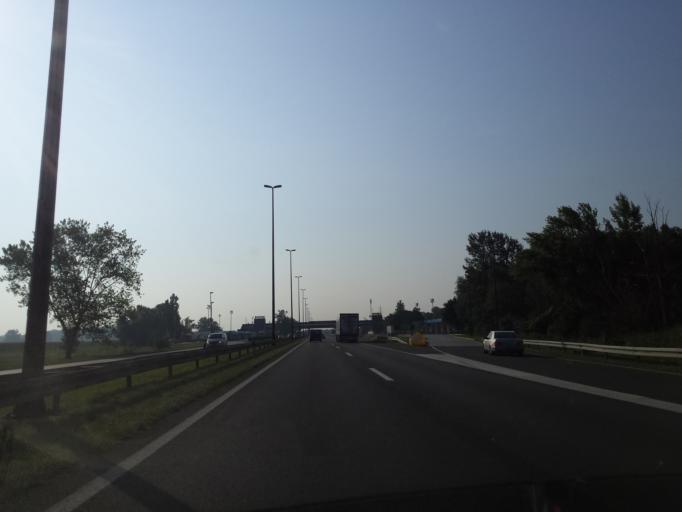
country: HR
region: Grad Zagreb
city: Lucko
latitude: 45.7767
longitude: 15.8753
